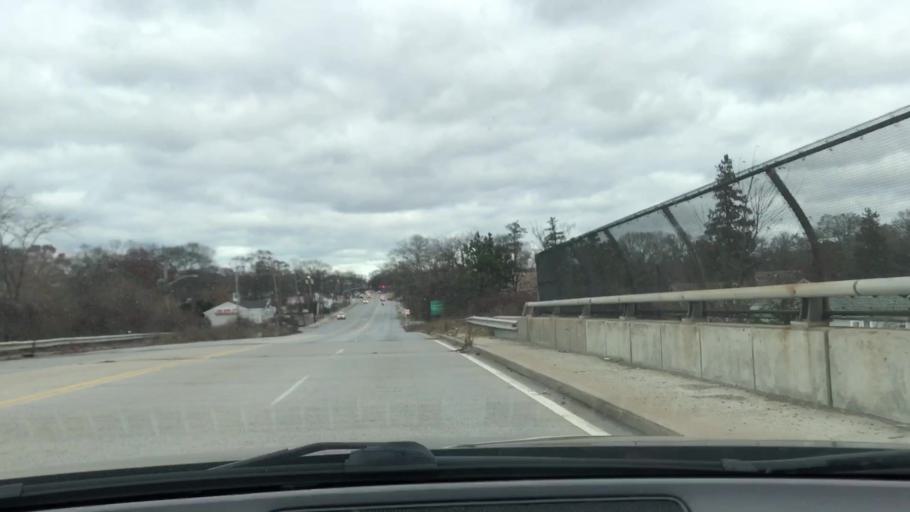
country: US
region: New York
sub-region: Suffolk County
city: Ronkonkoma
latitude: 40.8083
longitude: -73.1112
